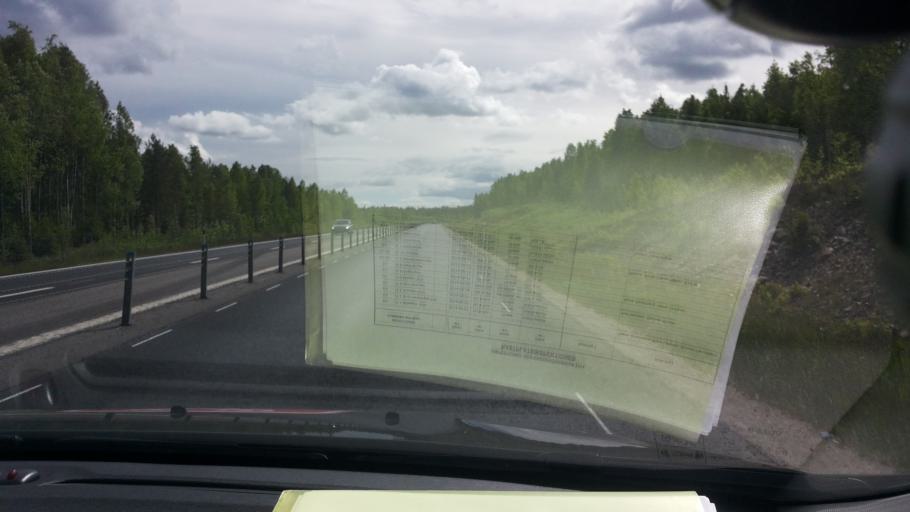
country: SE
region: Vaesternorrland
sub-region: Sundsvalls Kommun
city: Njurundabommen
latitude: 62.2022
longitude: 17.3718
